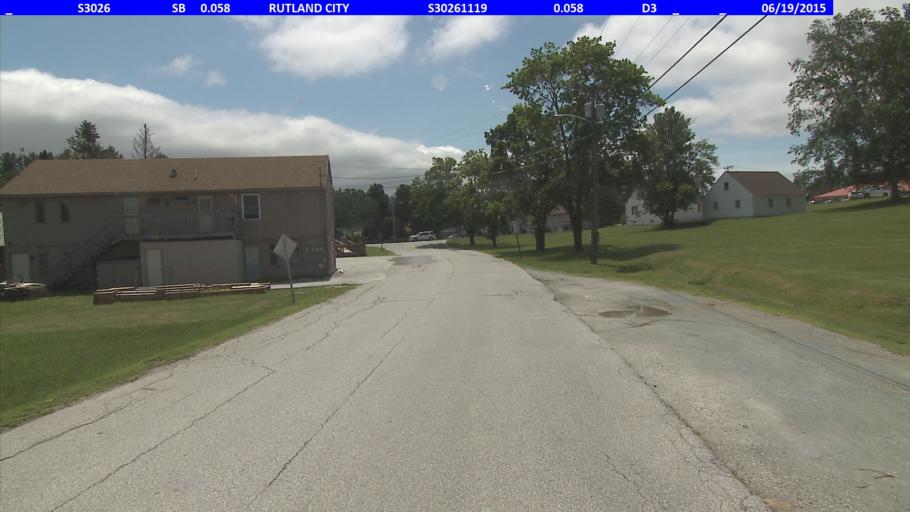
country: US
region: Vermont
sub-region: Rutland County
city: Rutland
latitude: 43.6177
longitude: -72.9595
